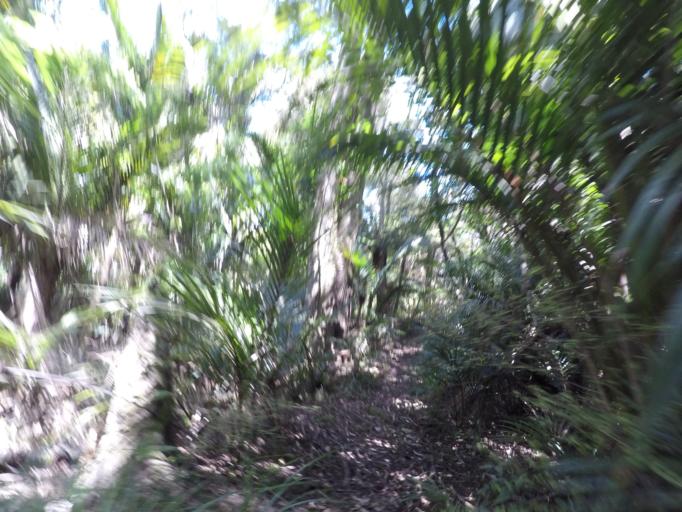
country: NZ
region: Auckland
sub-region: Auckland
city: Titirangi
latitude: -36.9749
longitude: 174.6306
